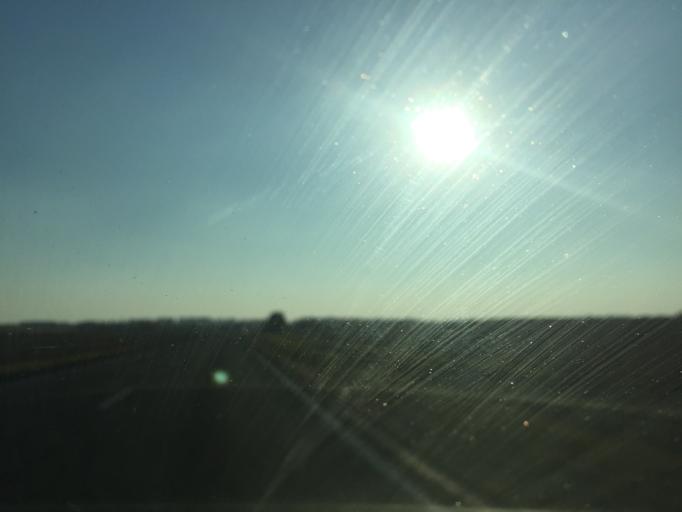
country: BY
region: Gomel
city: Dobrush
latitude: 52.3113
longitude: 31.2418
